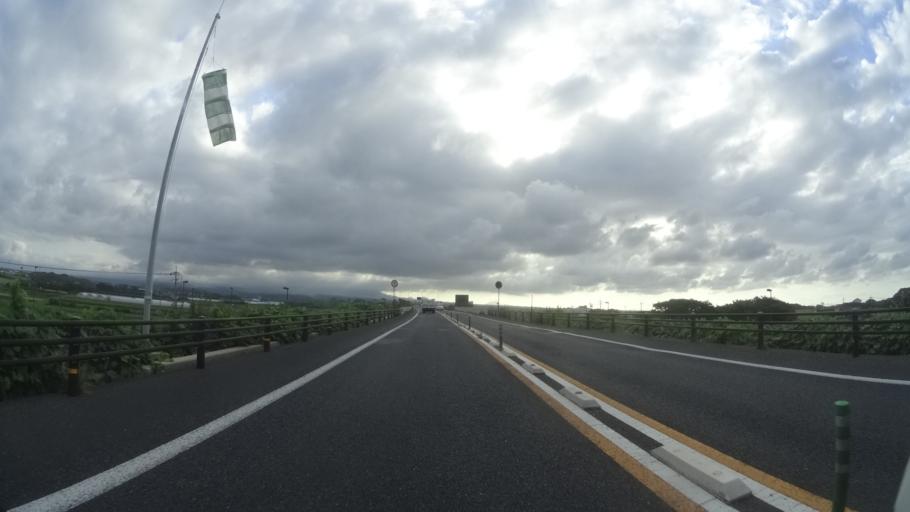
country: JP
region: Tottori
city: Kurayoshi
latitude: 35.5003
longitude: 133.7192
